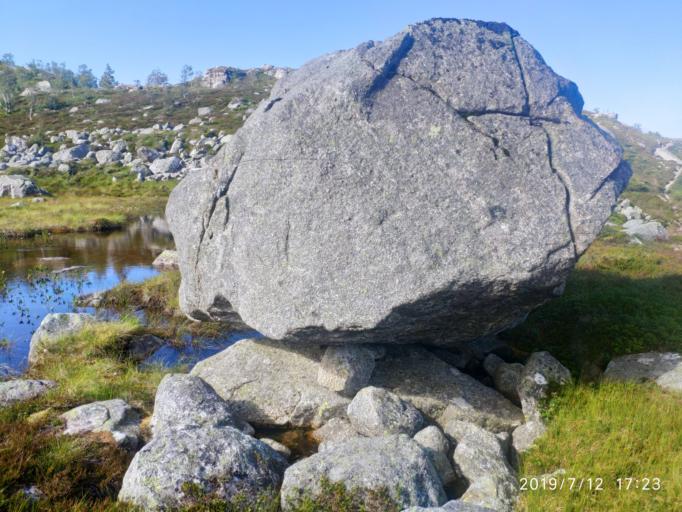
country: NO
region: Rogaland
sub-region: Forsand
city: Forsand
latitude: 58.9938
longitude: 6.1701
